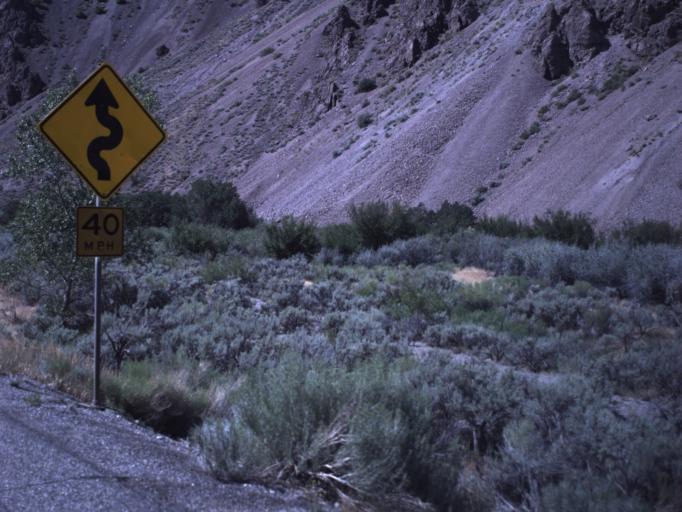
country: US
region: Utah
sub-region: Sevier County
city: Monroe
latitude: 38.5001
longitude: -112.2574
